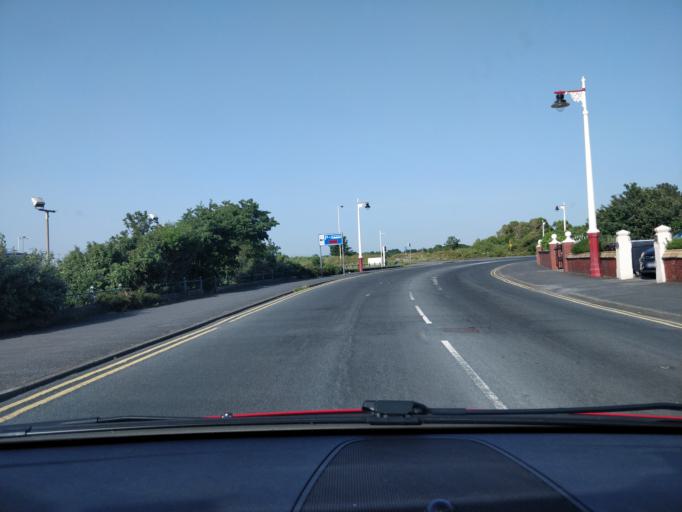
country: GB
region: England
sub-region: Sefton
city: Southport
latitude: 53.6590
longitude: -2.9990
